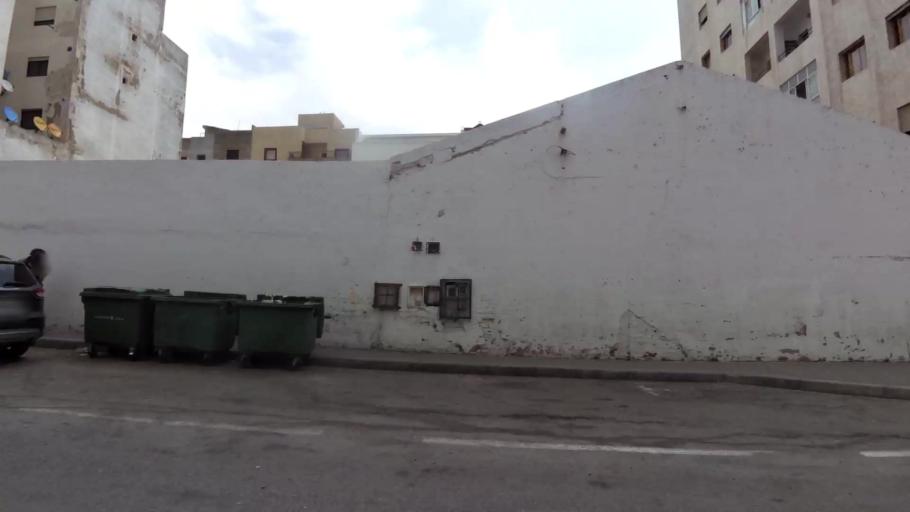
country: MA
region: Tanger-Tetouan
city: Tetouan
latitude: 35.5635
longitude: -5.3687
